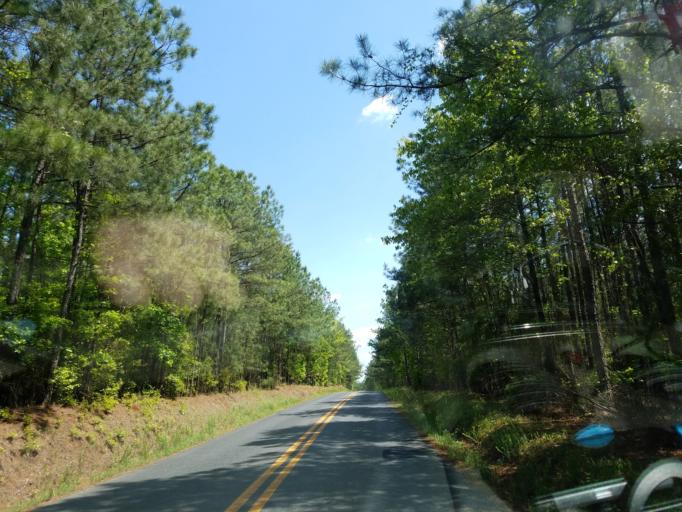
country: US
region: Georgia
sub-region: Monroe County
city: Forsyth
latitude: 33.1440
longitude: -84.0046
